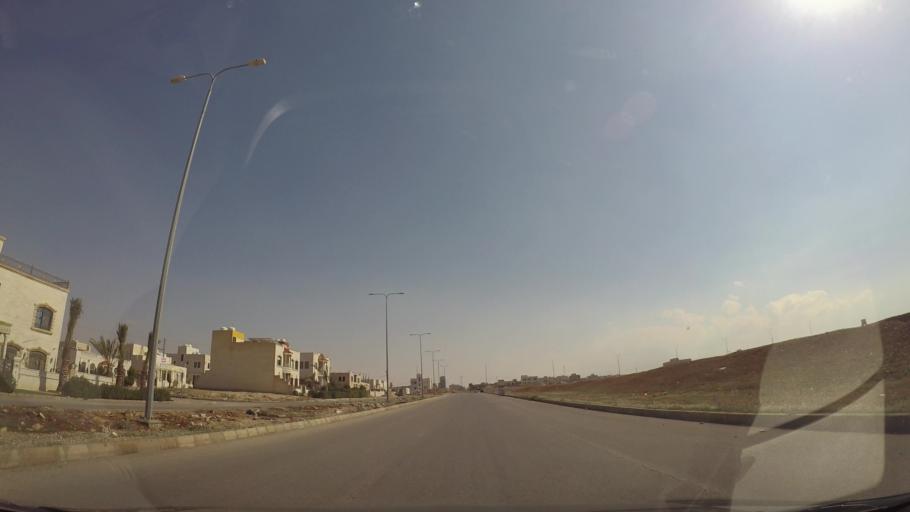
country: JO
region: Zarqa
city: Zarqa
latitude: 32.0565
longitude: 36.1146
